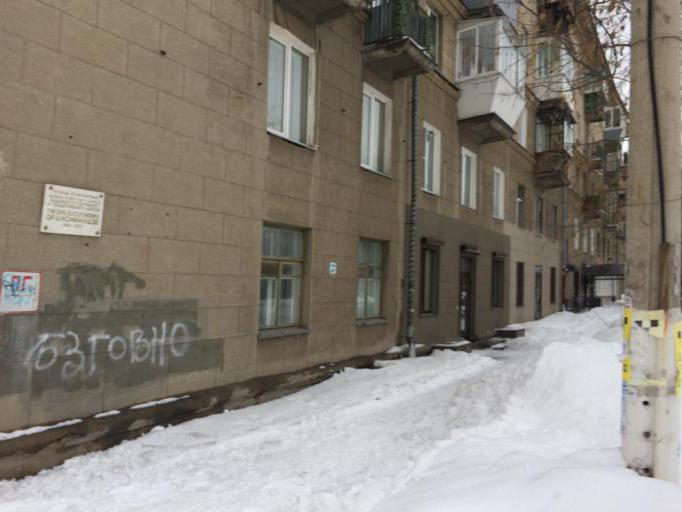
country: RU
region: Chelyabinsk
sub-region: Gorod Magnitogorsk
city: Magnitogorsk
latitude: 53.4177
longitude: 59.0013
